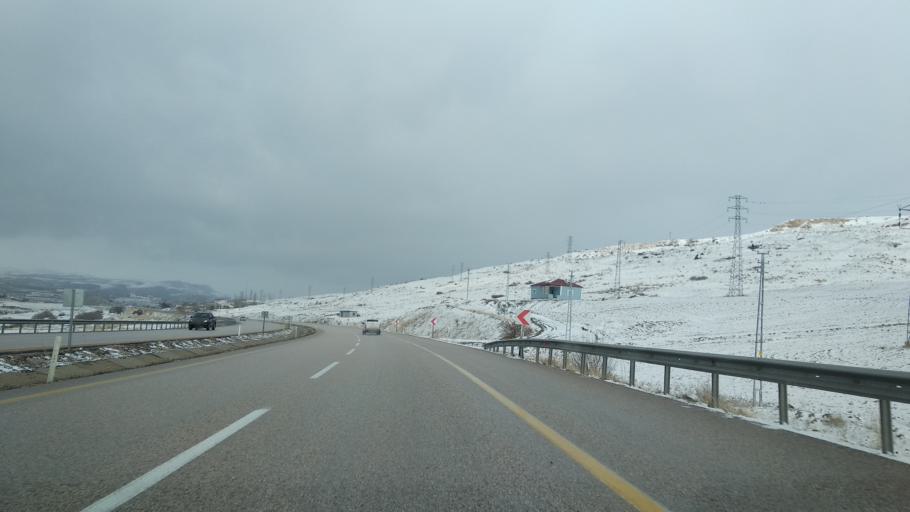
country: TR
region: Kayseri
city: Pinarbasi
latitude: 38.7022
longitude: 36.3726
